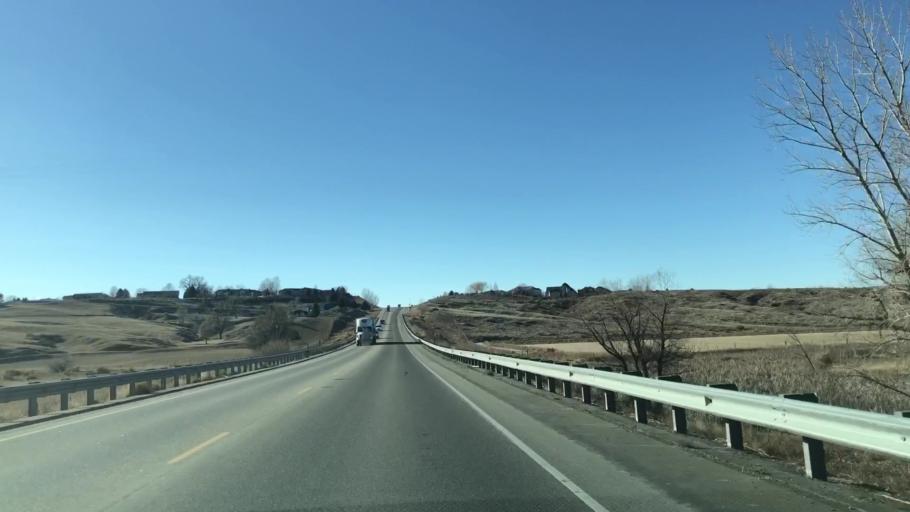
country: US
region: Colorado
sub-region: Weld County
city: Windsor
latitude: 40.4794
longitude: -104.9562
